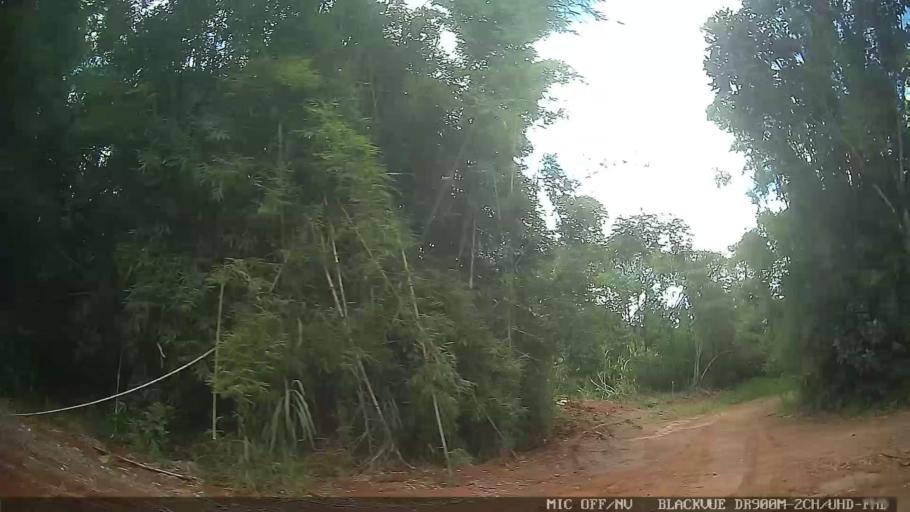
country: BR
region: Sao Paulo
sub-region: Bom Jesus Dos Perdoes
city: Bom Jesus dos Perdoes
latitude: -23.0382
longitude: -46.4843
